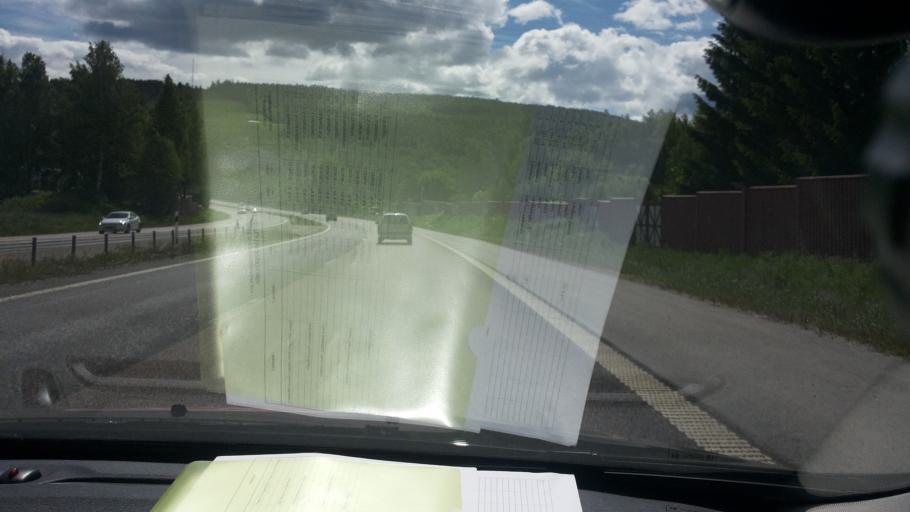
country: SE
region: Vaesternorrland
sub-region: Timra Kommun
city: Timra
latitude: 62.4758
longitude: 17.3114
